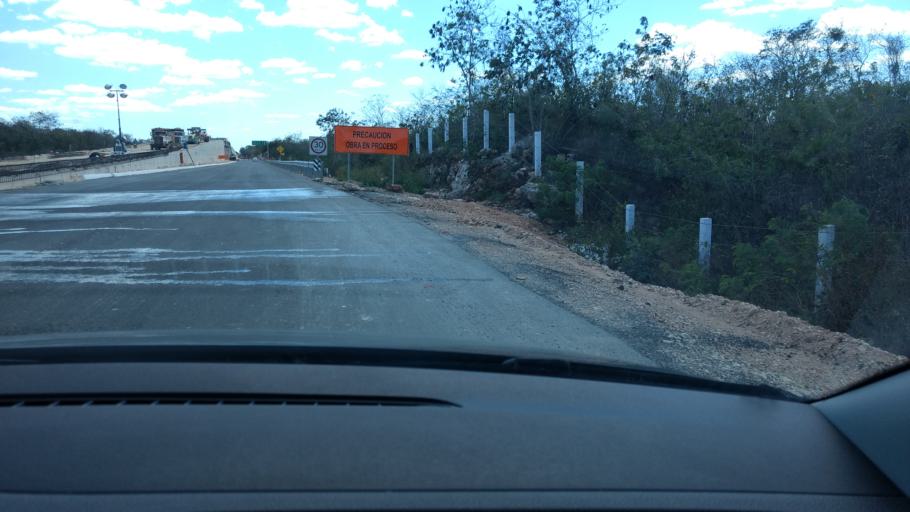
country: MX
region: Yucatan
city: Peto
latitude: 20.1216
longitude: -88.9492
